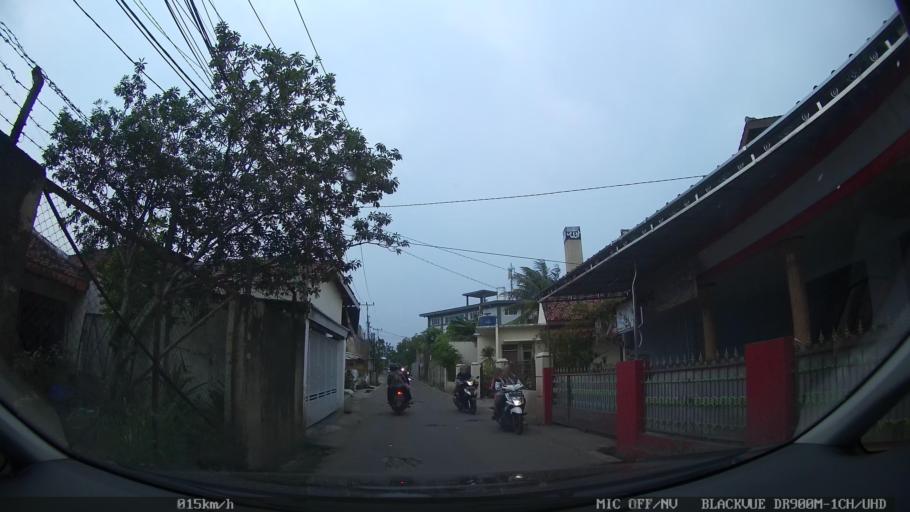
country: ID
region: Lampung
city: Kedaton
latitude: -5.4027
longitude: 105.2732
